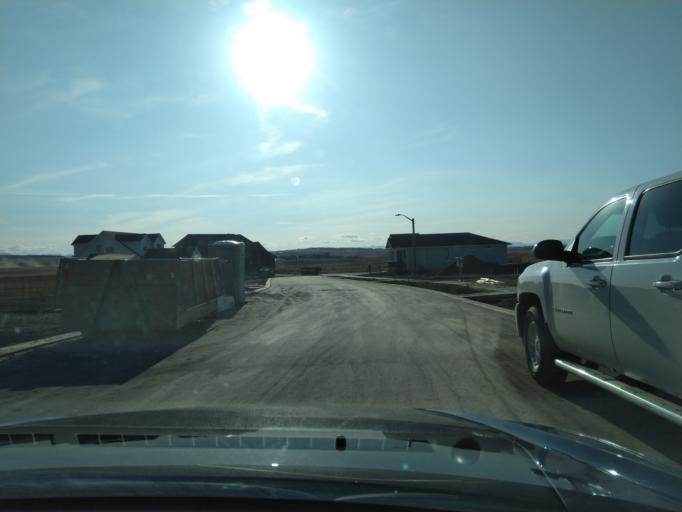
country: CA
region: Alberta
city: Cochrane
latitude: 51.1113
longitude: -114.4070
